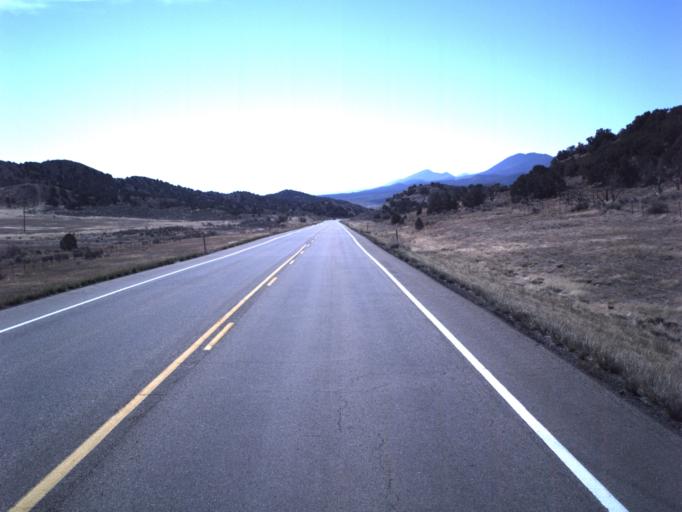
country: US
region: Utah
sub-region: Sanpete County
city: Gunnison
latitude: 39.3850
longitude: -111.9278
